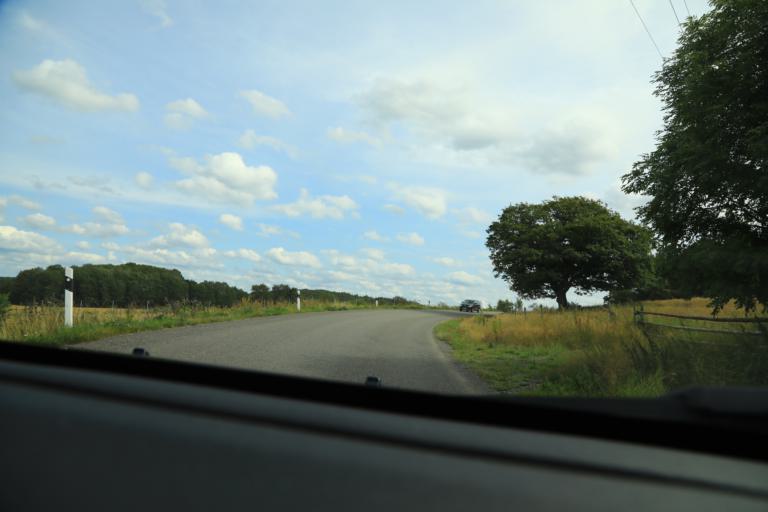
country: SE
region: Halland
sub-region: Varbergs Kommun
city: Varberg
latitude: 57.1768
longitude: 12.2716
